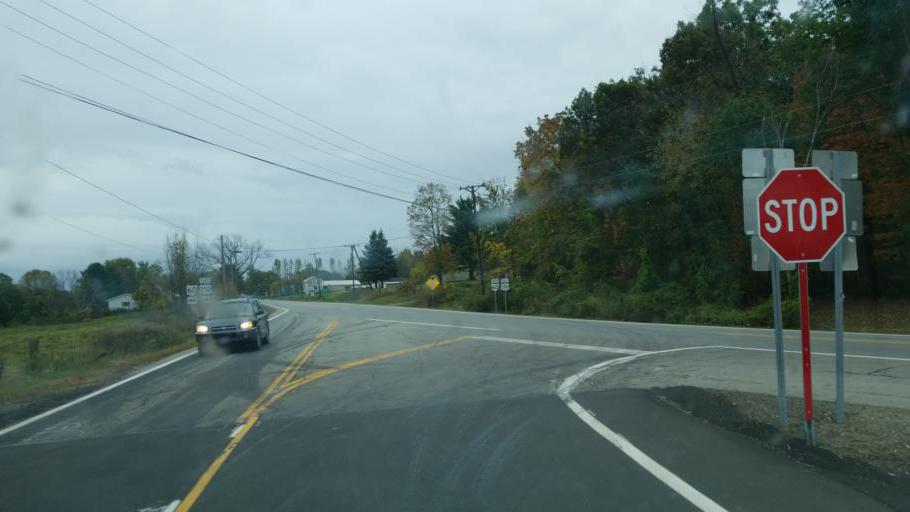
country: US
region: Ohio
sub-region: Huron County
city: New London
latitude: 40.9748
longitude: -82.3670
